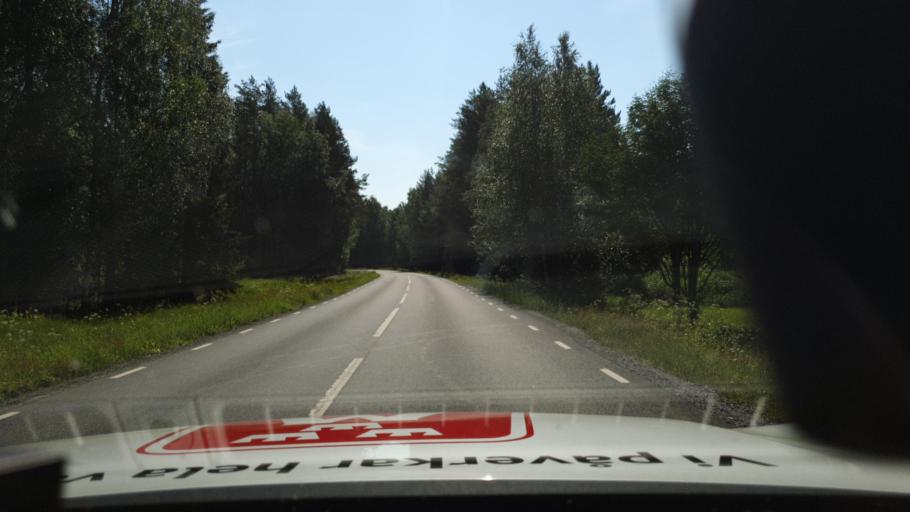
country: SE
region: Norrbotten
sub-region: Lulea Kommun
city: Gammelstad
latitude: 65.7890
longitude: 22.0852
